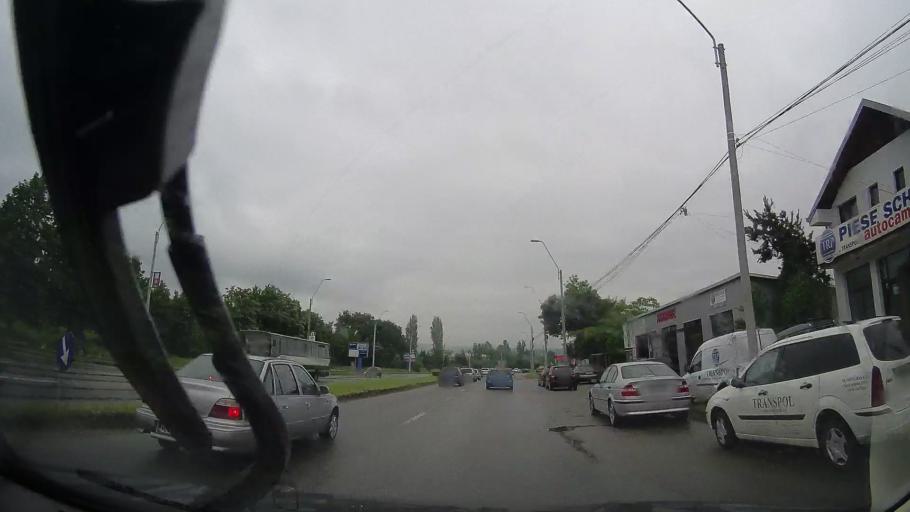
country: RO
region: Mehedinti
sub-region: Municipiul Drobeta-Turnu Severin
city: Drobeta-Turnu Severin
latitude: 44.6324
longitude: 22.6813
